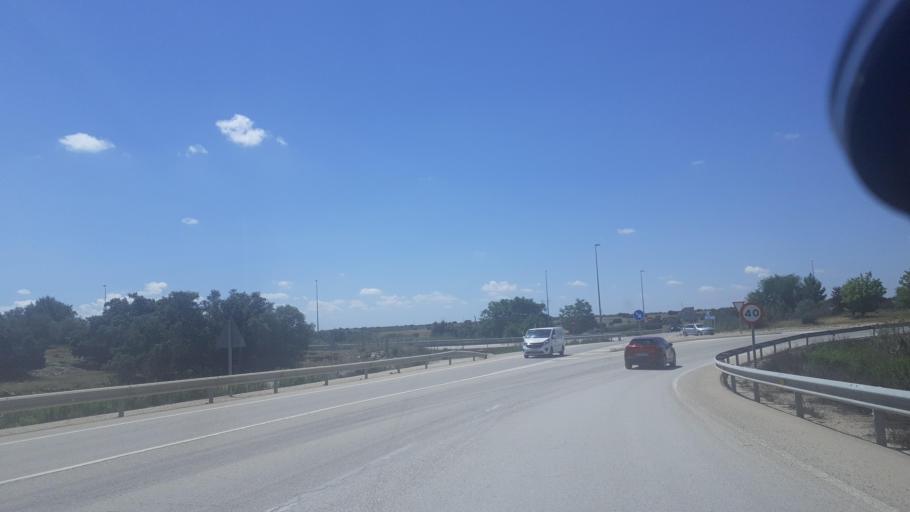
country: ES
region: Madrid
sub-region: Provincia de Madrid
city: Perales de Tajuna
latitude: 40.2567
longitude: -3.3756
